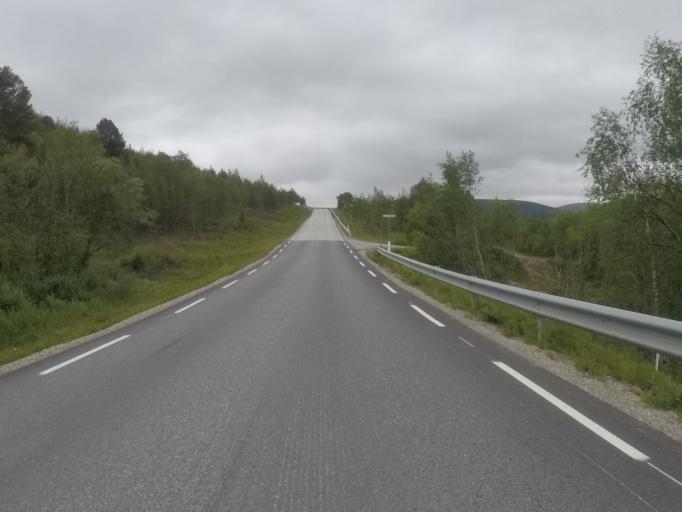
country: NO
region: Finnmark Fylke
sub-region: Karasjok
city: Karasjohka
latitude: 69.5730
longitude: 25.9141
